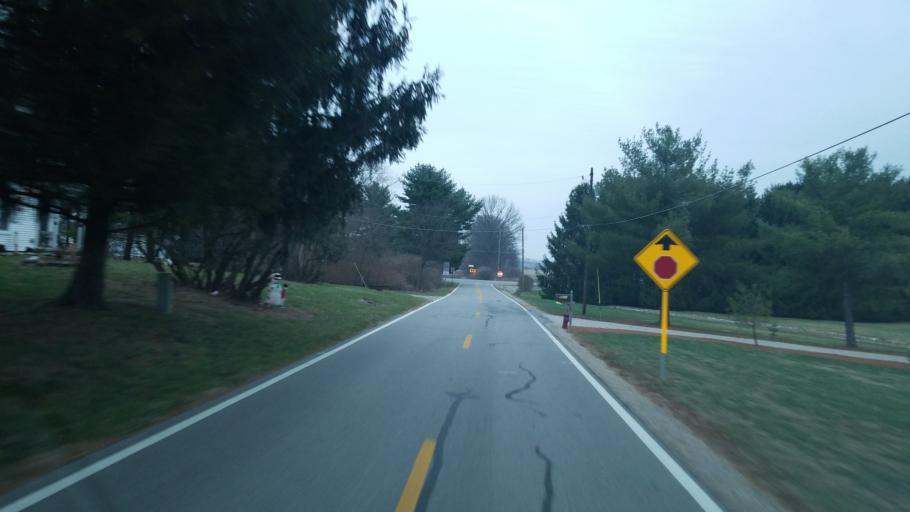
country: US
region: Ohio
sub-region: Delaware County
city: Sunbury
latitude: 40.2840
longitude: -82.9098
